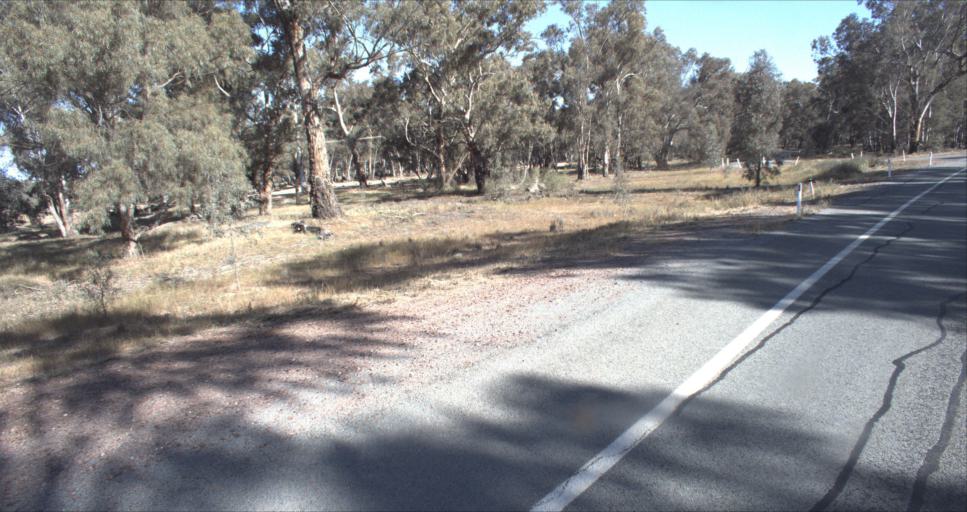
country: AU
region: New South Wales
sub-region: Leeton
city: Leeton
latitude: -34.6366
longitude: 146.3755
